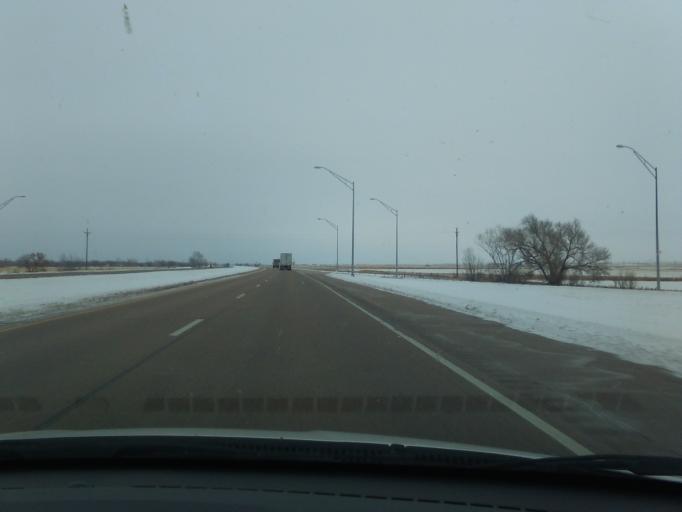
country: US
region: Nebraska
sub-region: Keith County
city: Ogallala
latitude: 41.0796
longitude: -101.8853
